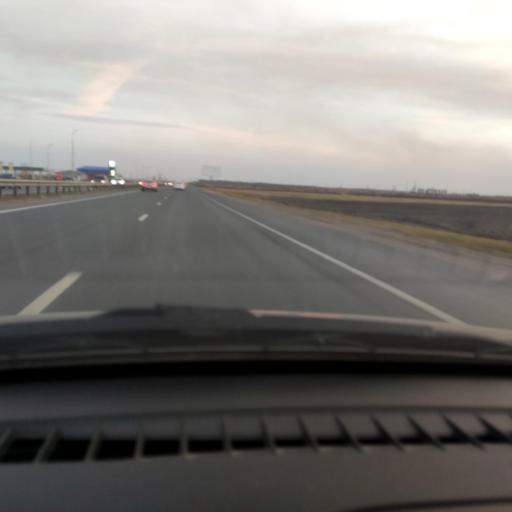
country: RU
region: Samara
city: Tol'yatti
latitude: 53.5586
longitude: 49.5012
